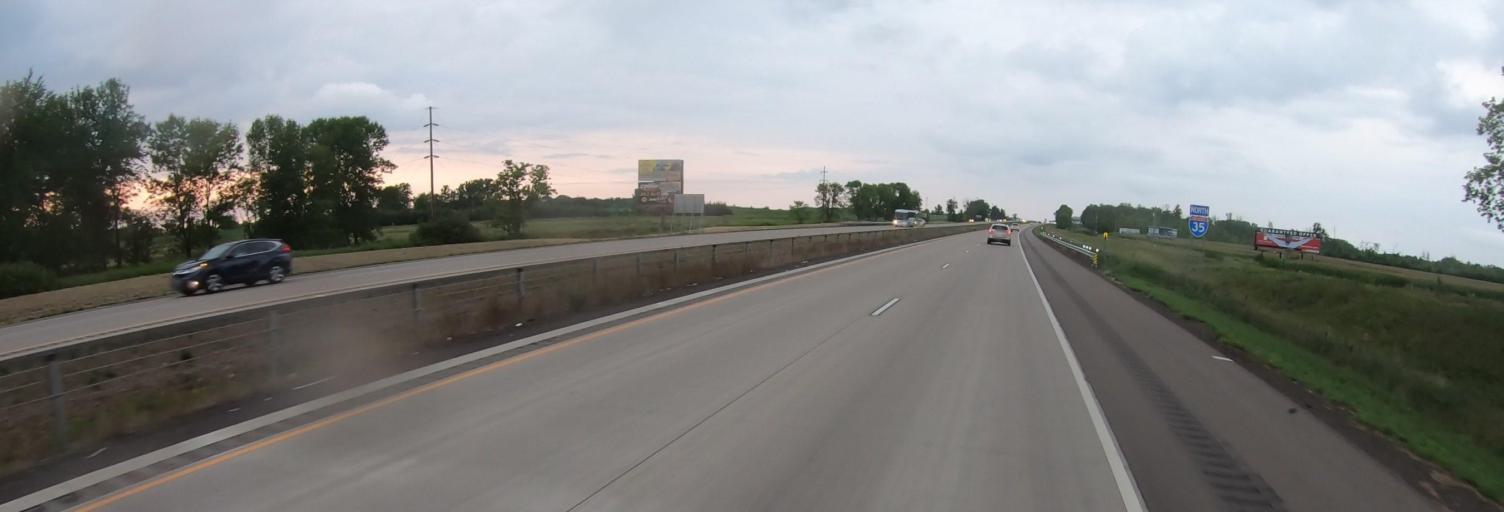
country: US
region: Minnesota
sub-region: Pine County
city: Rock Creek
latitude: 45.7732
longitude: -92.9895
